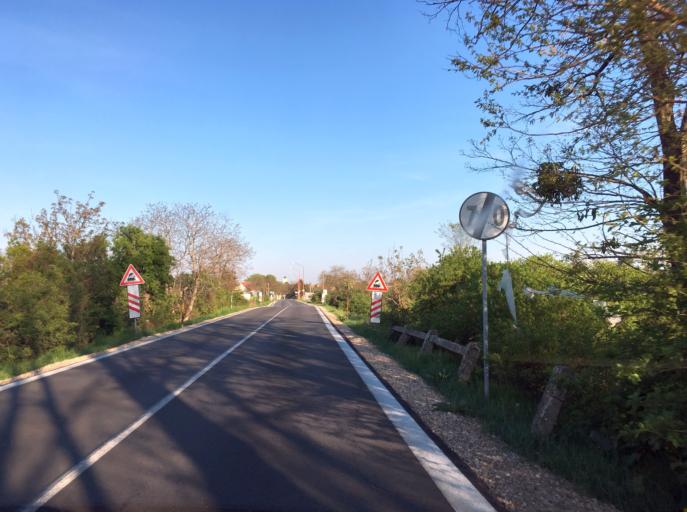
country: AT
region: Burgenland
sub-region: Politischer Bezirk Neusiedl am See
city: Deutsch Jahrndorf
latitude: 48.0590
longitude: 17.1348
